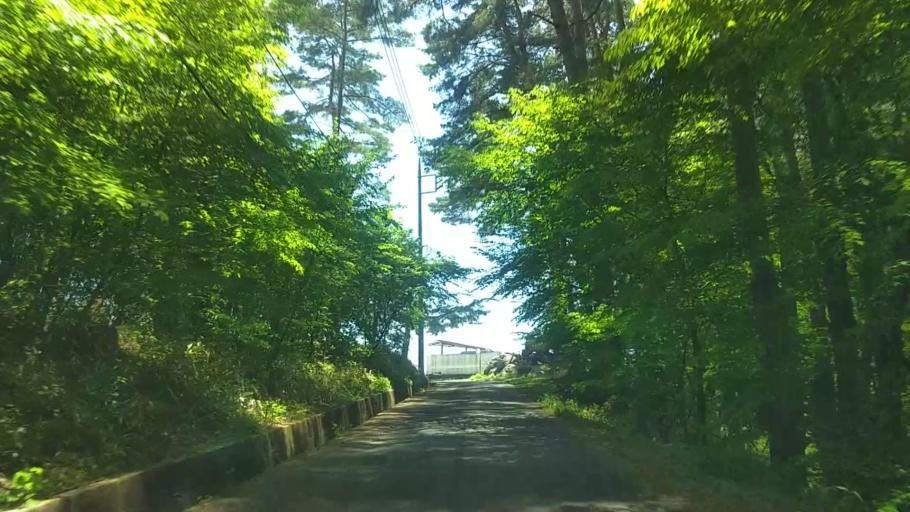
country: JP
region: Yamanashi
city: Nirasaki
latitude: 35.8882
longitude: 138.4342
